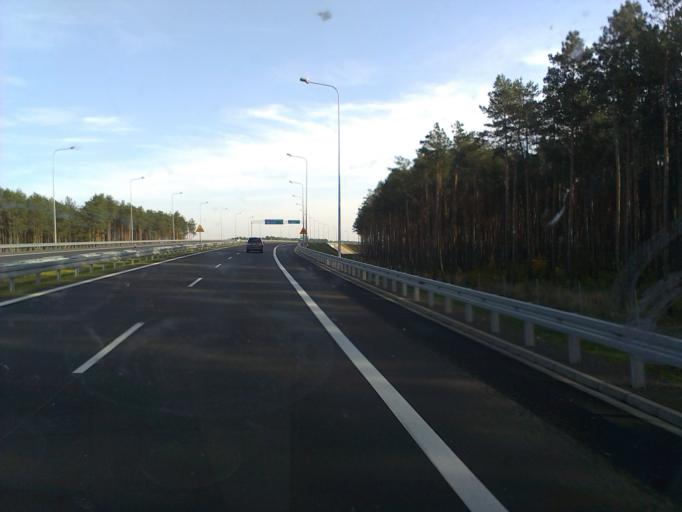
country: PL
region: Lubusz
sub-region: Powiat miedzyrzecki
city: Skwierzyna
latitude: 52.5606
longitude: 15.5108
